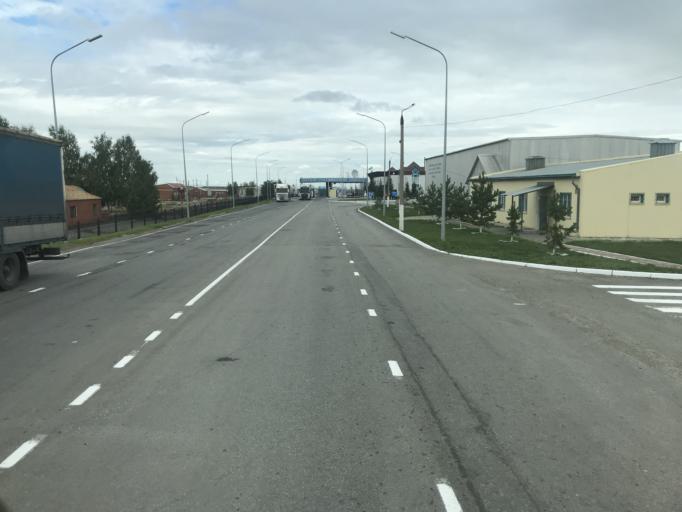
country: RU
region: Chelyabinsk
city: Bobrovka
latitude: 53.9992
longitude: 61.6408
